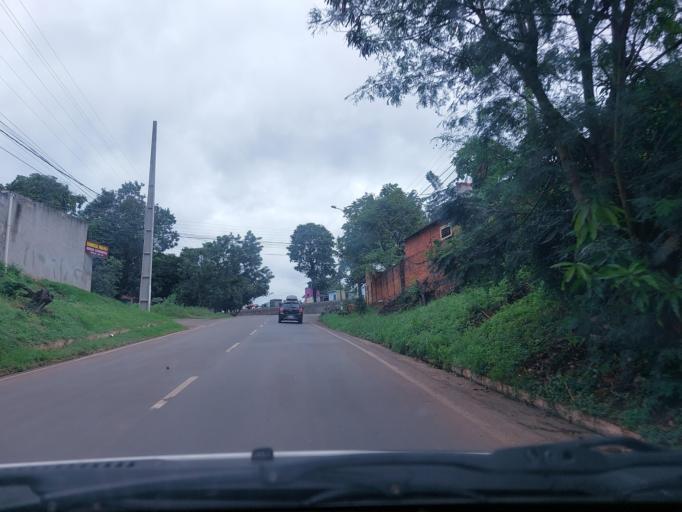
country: PY
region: San Pedro
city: Guayaybi
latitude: -24.6691
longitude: -56.4417
